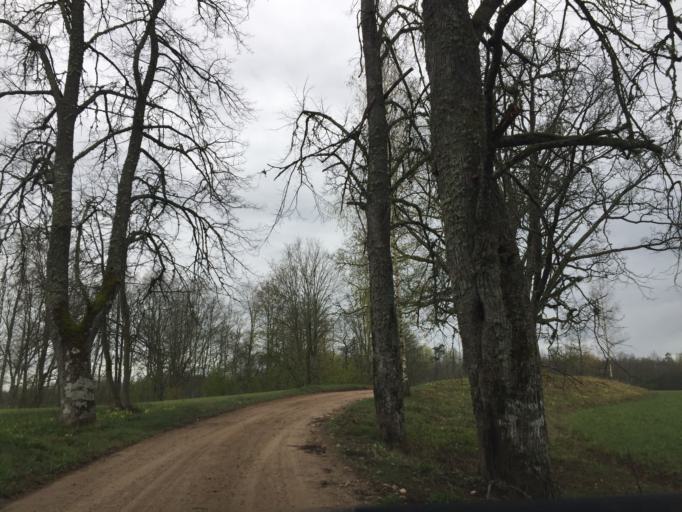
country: LV
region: Sigulda
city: Sigulda
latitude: 57.0322
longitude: 24.8429
